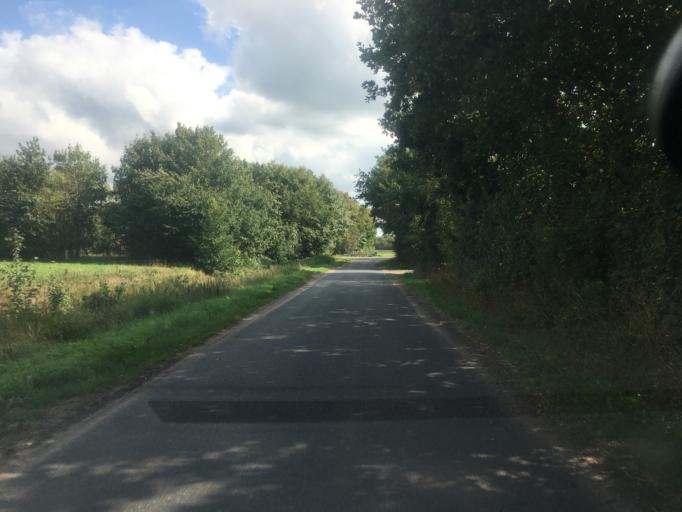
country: DK
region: South Denmark
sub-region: Tonder Kommune
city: Logumkloster
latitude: 55.0014
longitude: 9.0147
